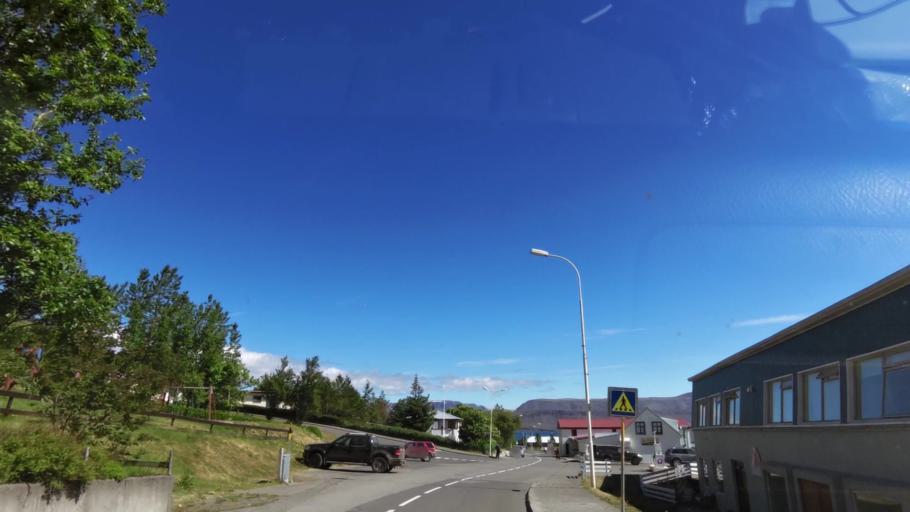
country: IS
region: Westfjords
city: Isafjoerdur
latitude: 65.6852
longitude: -23.6023
